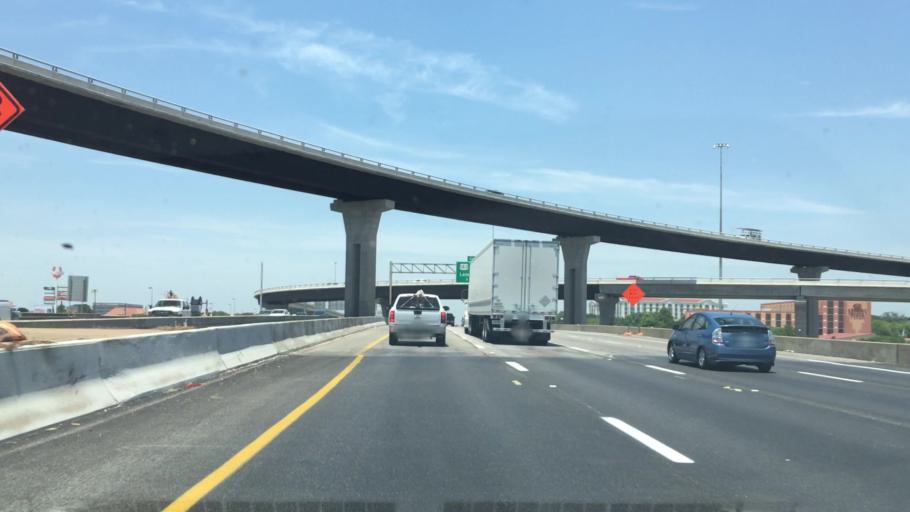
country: US
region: Texas
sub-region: Travis County
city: Austin
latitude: 30.3212
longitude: -97.7069
